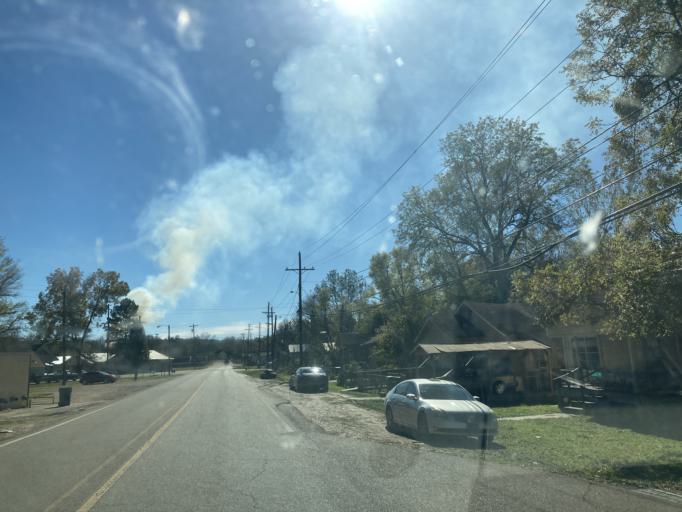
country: US
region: Mississippi
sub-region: Yazoo County
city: Yazoo City
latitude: 32.8553
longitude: -90.4112
